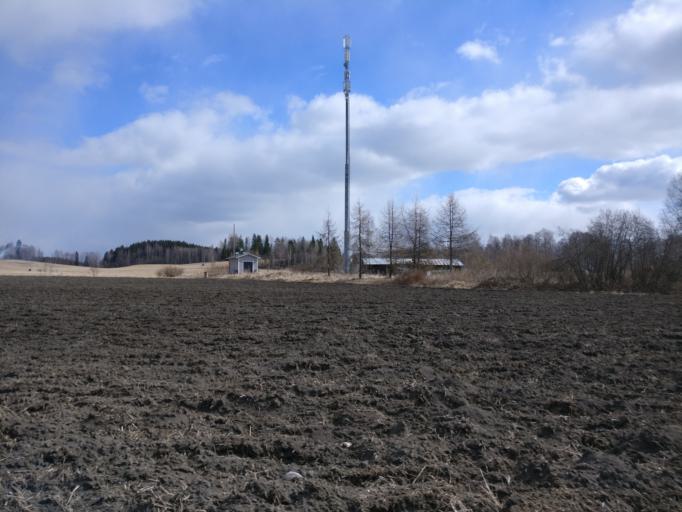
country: FI
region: Uusimaa
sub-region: Helsinki
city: Karjalohja
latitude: 60.2414
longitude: 23.7389
